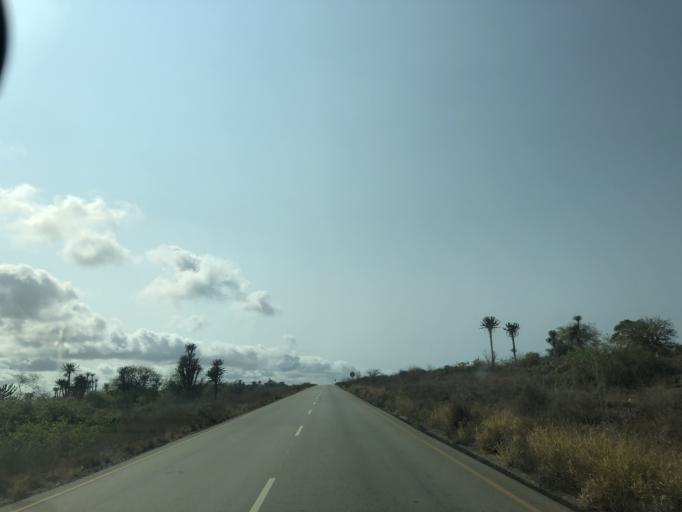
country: AO
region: Luanda
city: Luanda
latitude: -9.7008
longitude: 13.2129
